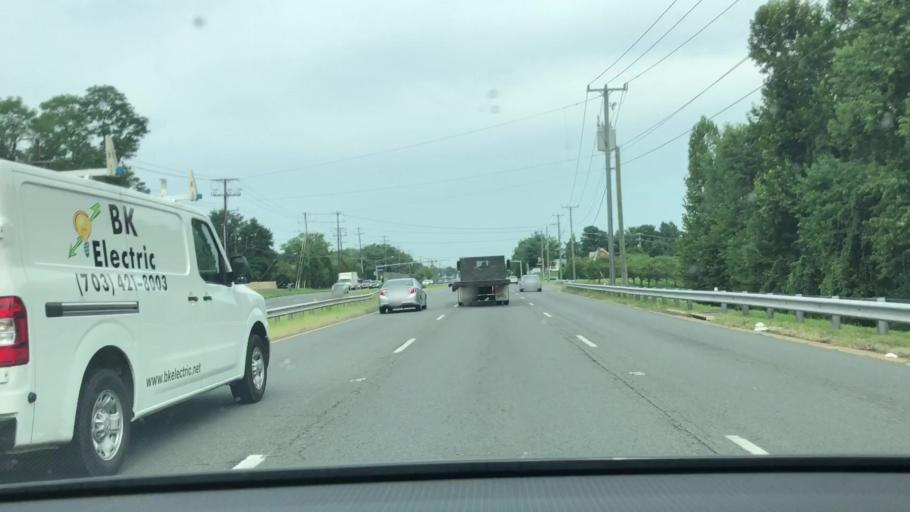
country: US
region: Virginia
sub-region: Fairfax County
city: Greenbriar
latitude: 38.8864
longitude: -77.4110
